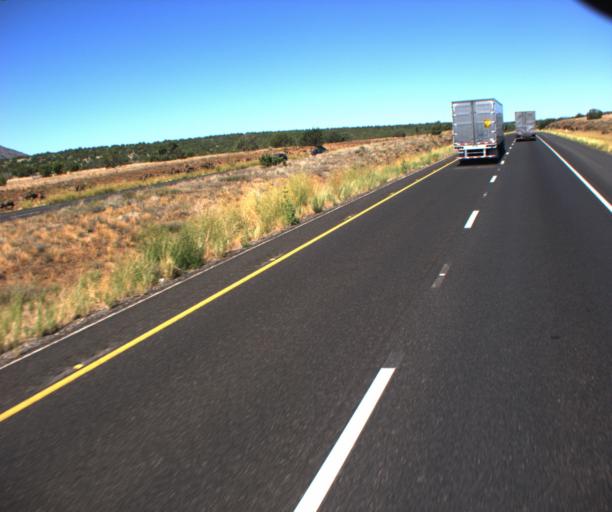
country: US
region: Arizona
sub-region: Yavapai County
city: Paulden
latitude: 35.2504
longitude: -112.6908
